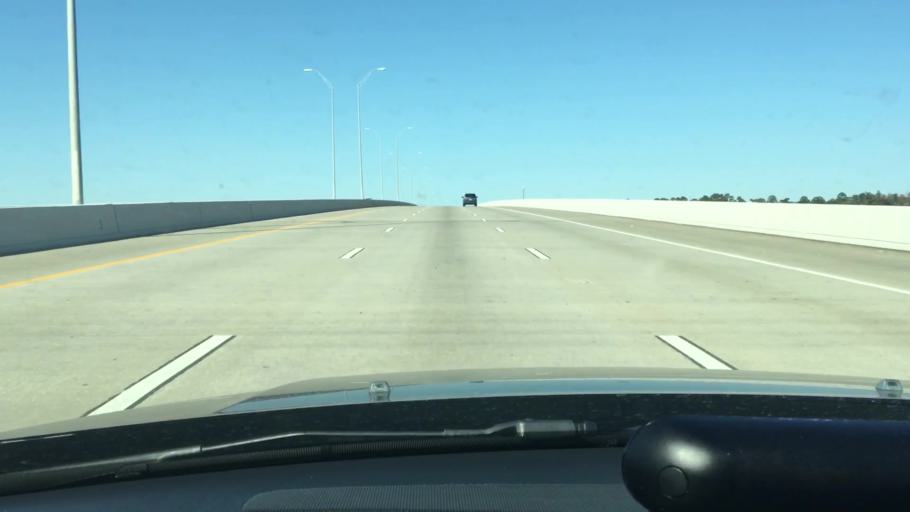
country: US
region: Texas
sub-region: Harris County
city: Cloverleaf
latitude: 29.8307
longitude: -95.1739
